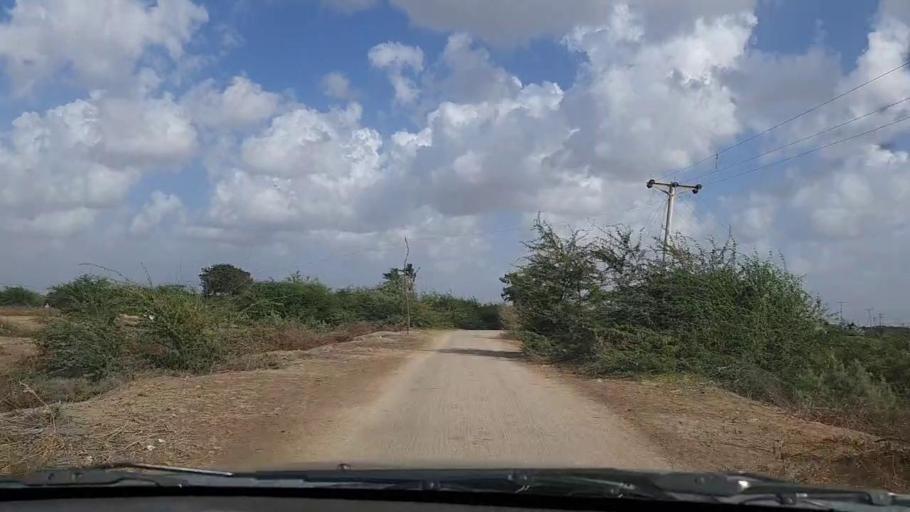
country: PK
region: Sindh
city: Keti Bandar
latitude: 24.0949
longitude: 67.6109
